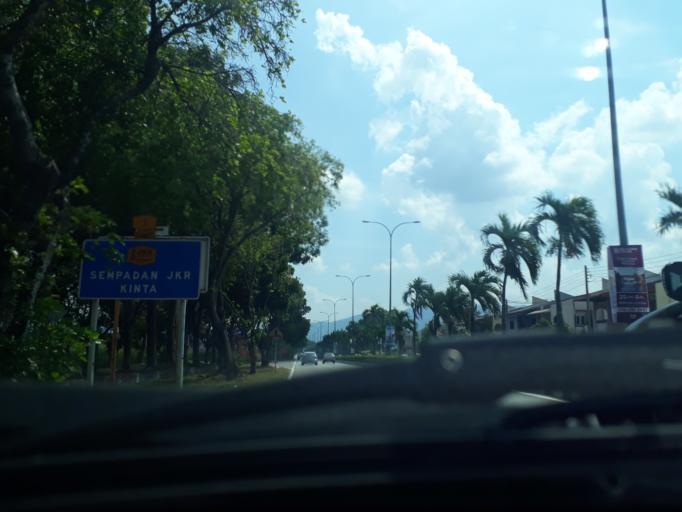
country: MY
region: Perak
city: Ipoh
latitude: 4.5775
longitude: 101.1011
